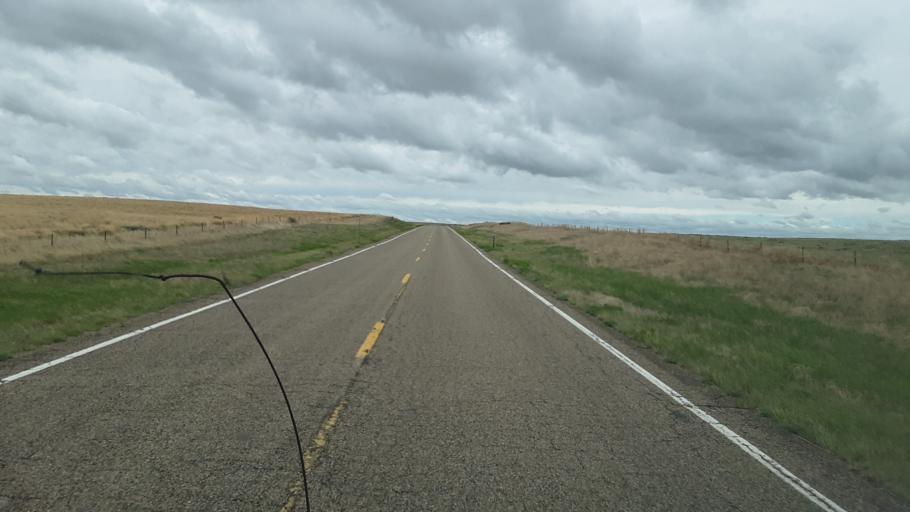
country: US
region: Colorado
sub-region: Lincoln County
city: Hugo
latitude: 38.8509
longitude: -103.5990
